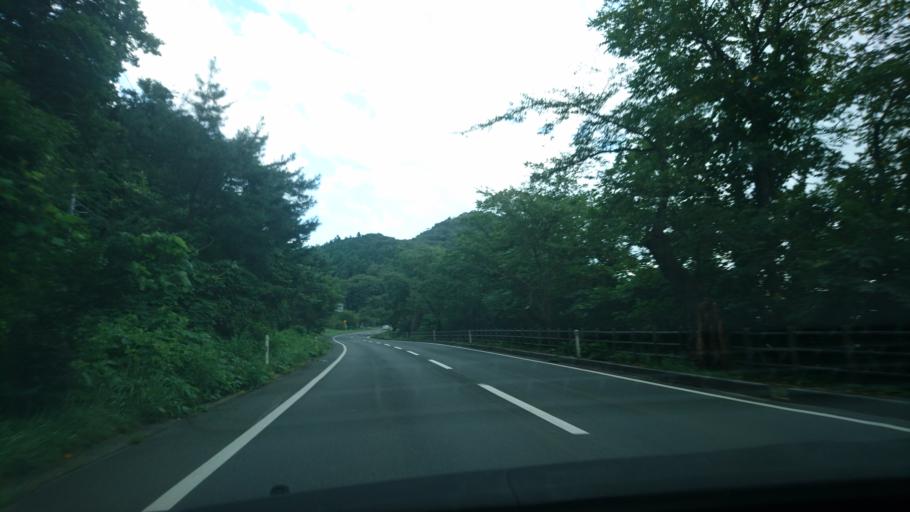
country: JP
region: Iwate
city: Kitakami
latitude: 39.2679
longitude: 141.1260
